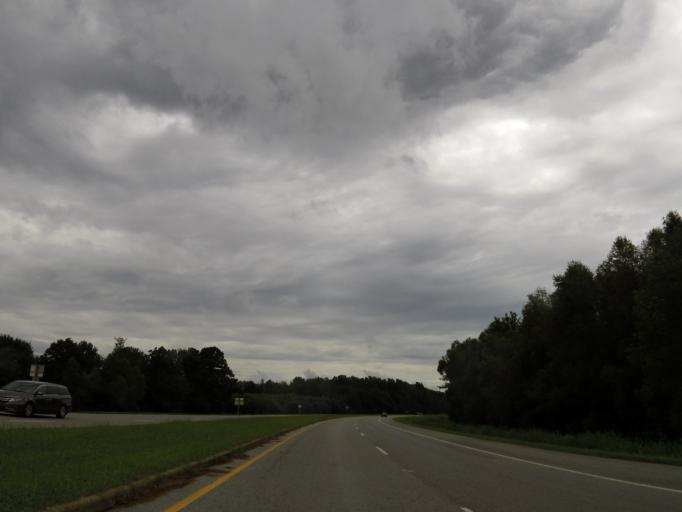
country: US
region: Illinois
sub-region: Alexander County
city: Cairo
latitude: 37.0375
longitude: -89.1874
